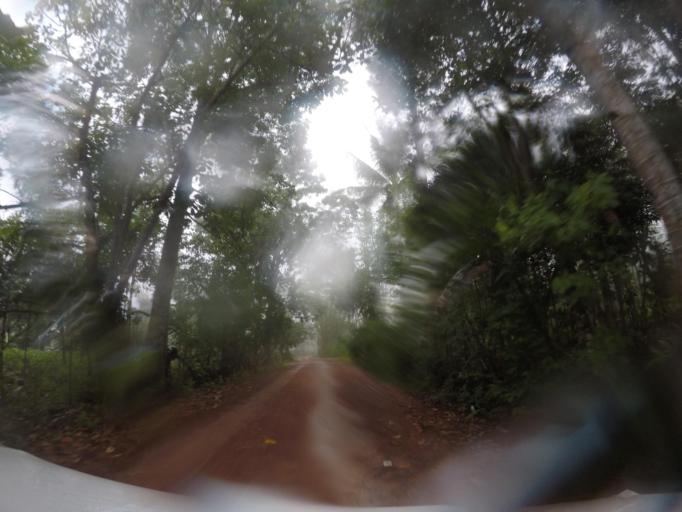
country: TL
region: Baucau
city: Venilale
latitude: -8.6381
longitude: 126.4184
